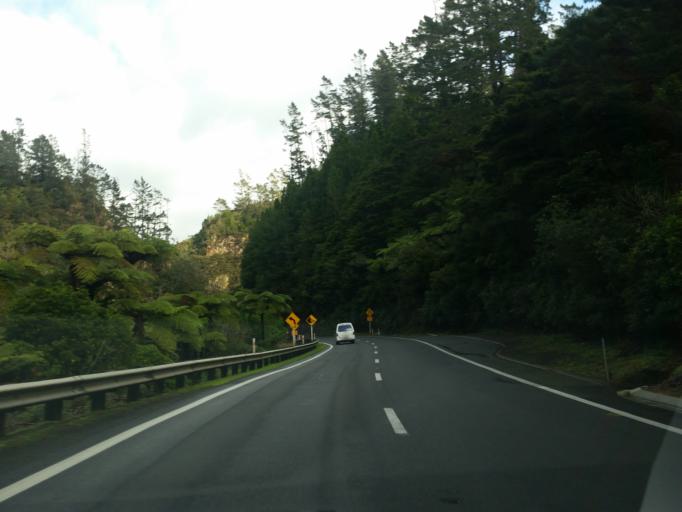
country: NZ
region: Waikato
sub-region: Hauraki District
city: Paeroa
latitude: -37.4202
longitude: 175.7353
